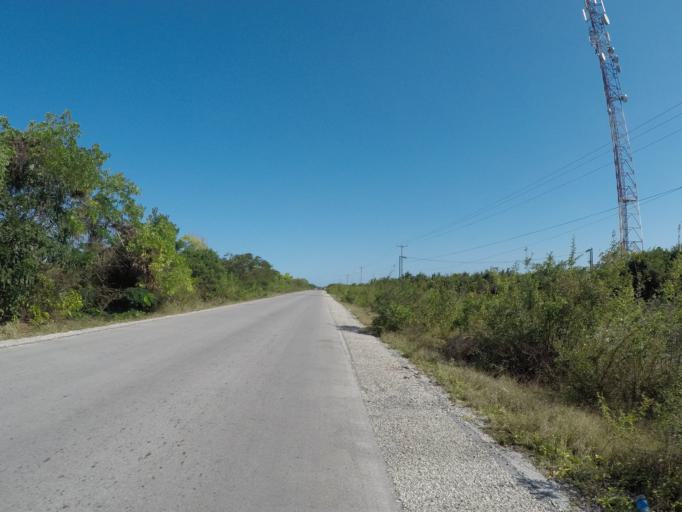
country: TZ
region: Zanzibar Central/South
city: Nganane
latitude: -6.1781
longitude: 39.5273
